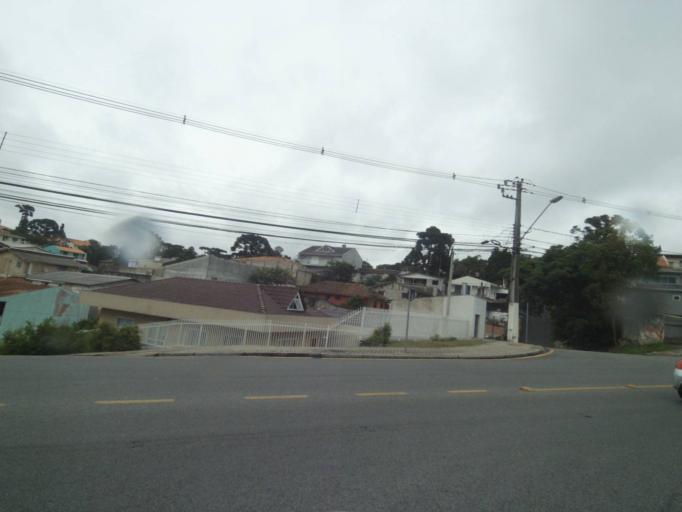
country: BR
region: Parana
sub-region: Curitiba
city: Curitiba
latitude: -25.4234
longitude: -49.3206
